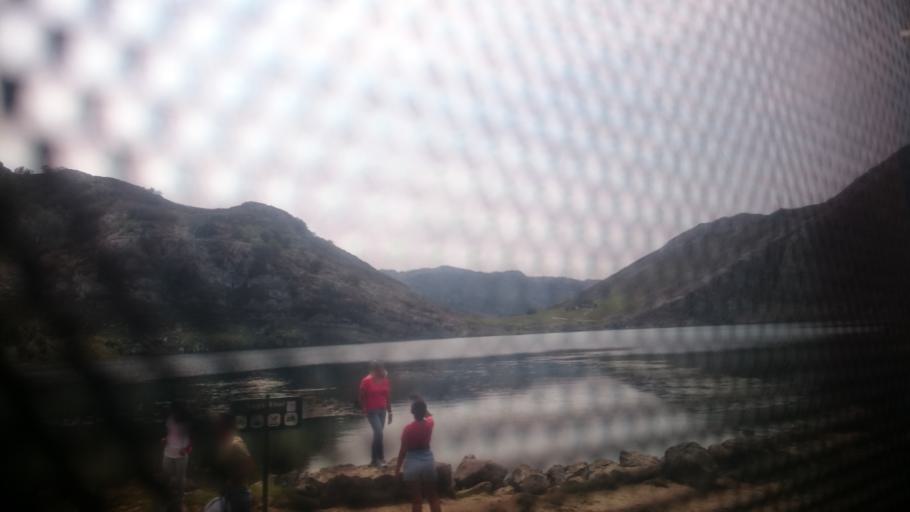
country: ES
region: Asturias
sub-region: Province of Asturias
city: Amieva
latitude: 43.2738
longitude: -4.9884
